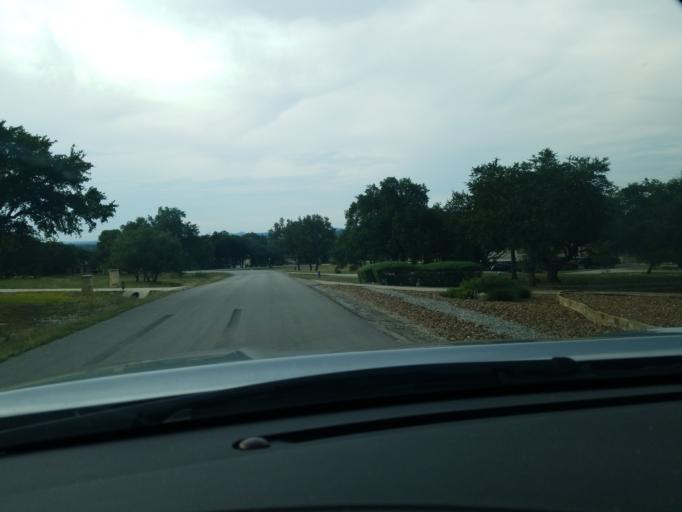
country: US
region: Texas
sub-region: Comal County
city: Bulverde
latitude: 29.8383
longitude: -98.4046
